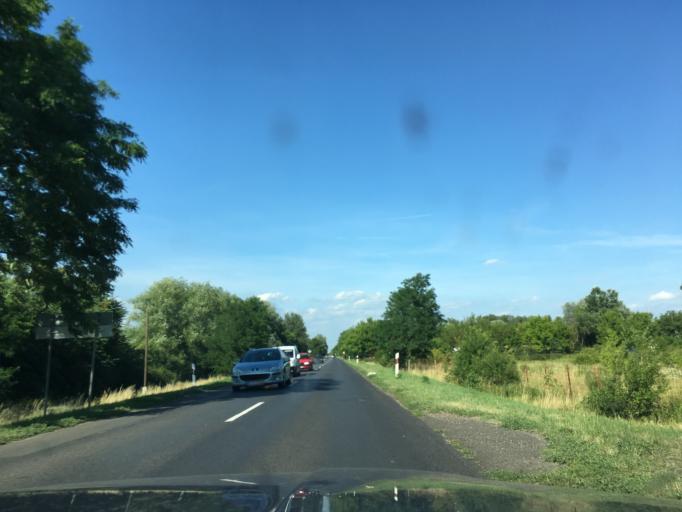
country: HU
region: Hajdu-Bihar
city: Debrecen
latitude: 47.5673
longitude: 21.6858
